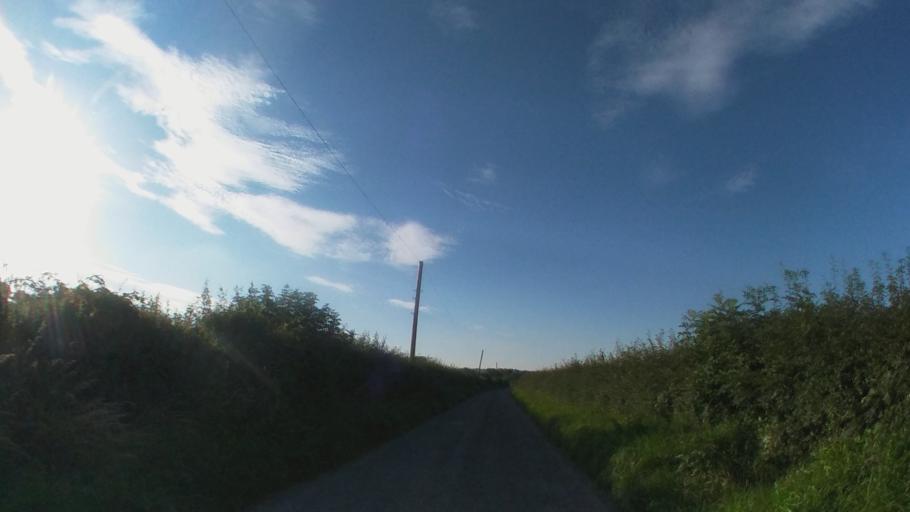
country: IE
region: Leinster
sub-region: Kilkenny
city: Kilkenny
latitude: 52.6930
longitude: -7.1897
